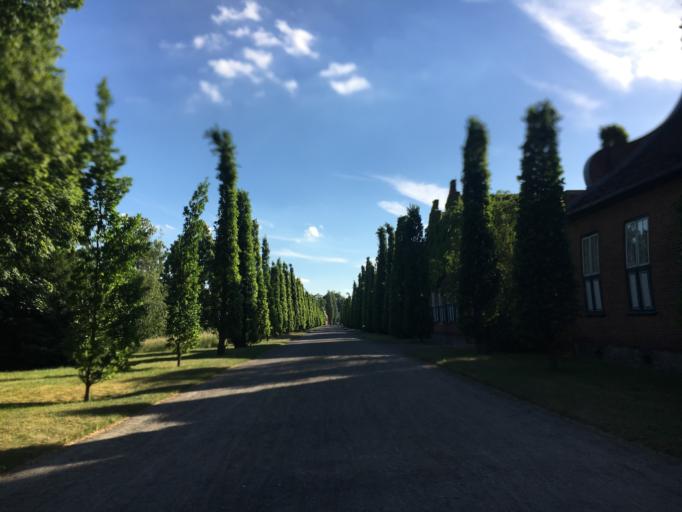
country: DE
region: Brandenburg
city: Potsdam
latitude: 52.4118
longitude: 13.0671
